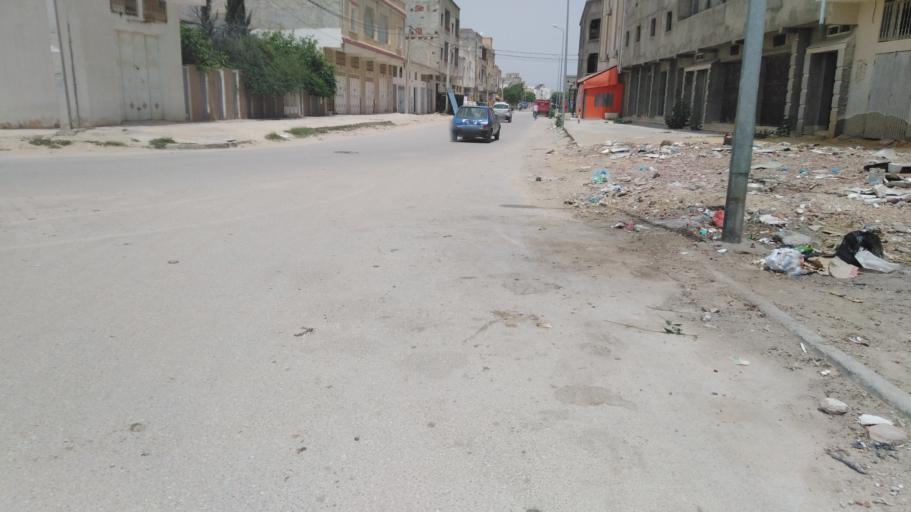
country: TN
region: Al Qayrawan
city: Kairouan
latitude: 35.6639
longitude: 10.0984
